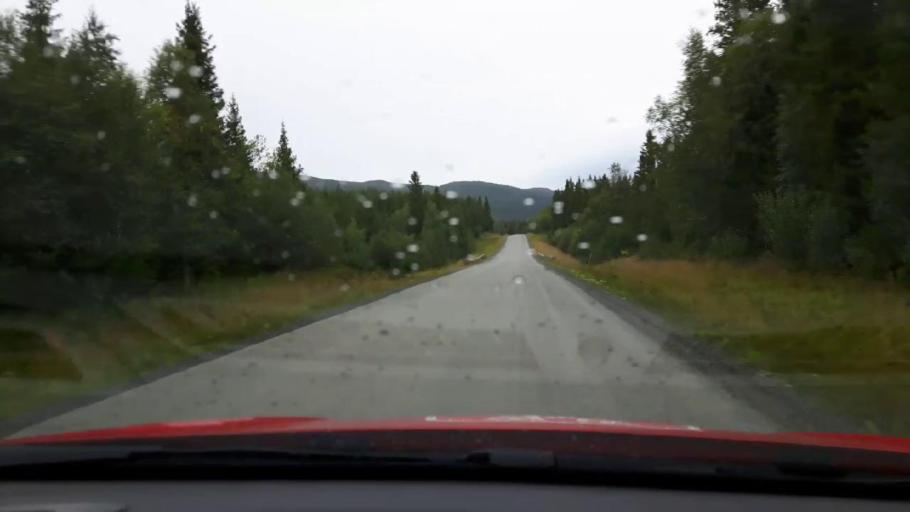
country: SE
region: Jaemtland
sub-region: Are Kommun
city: Are
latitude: 63.4491
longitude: 13.2195
